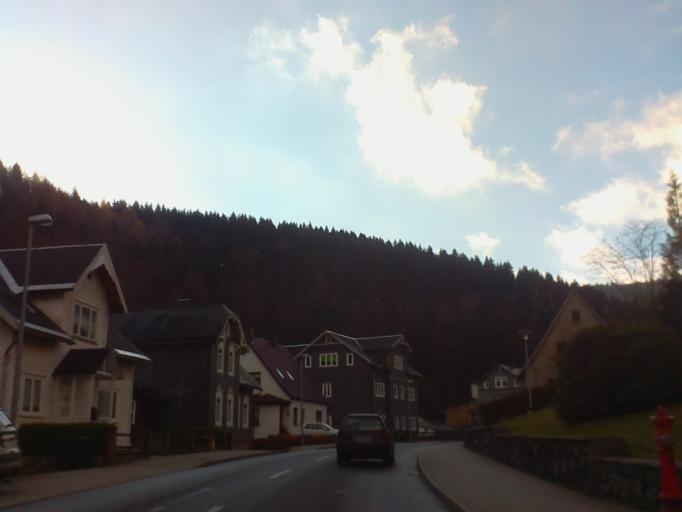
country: DE
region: Thuringia
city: Katzhutte
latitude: 50.5507
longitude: 11.0533
